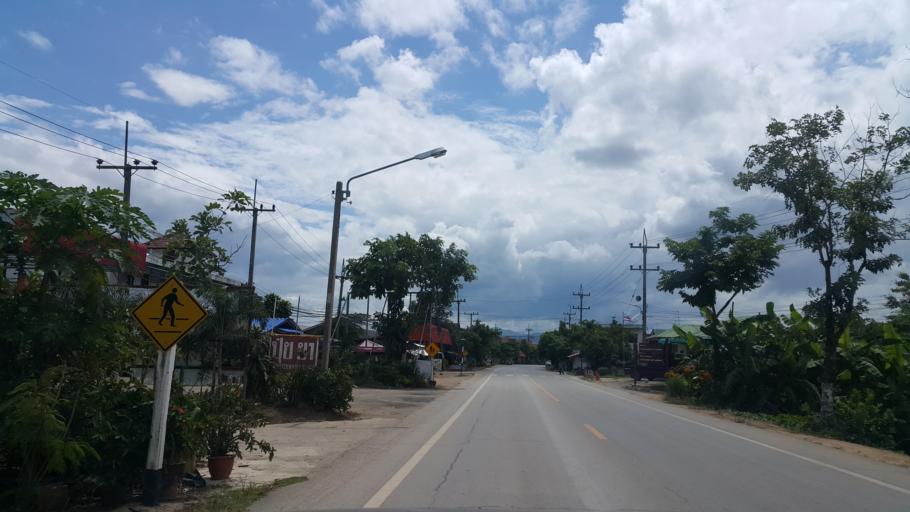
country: TH
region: Chiang Mai
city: Mae Taeng
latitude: 19.1450
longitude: 99.0138
